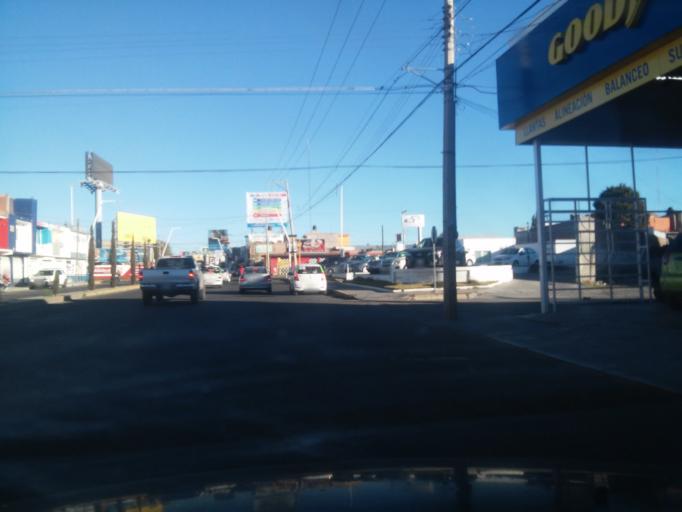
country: MX
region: Durango
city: Victoria de Durango
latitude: 24.0191
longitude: -104.6517
